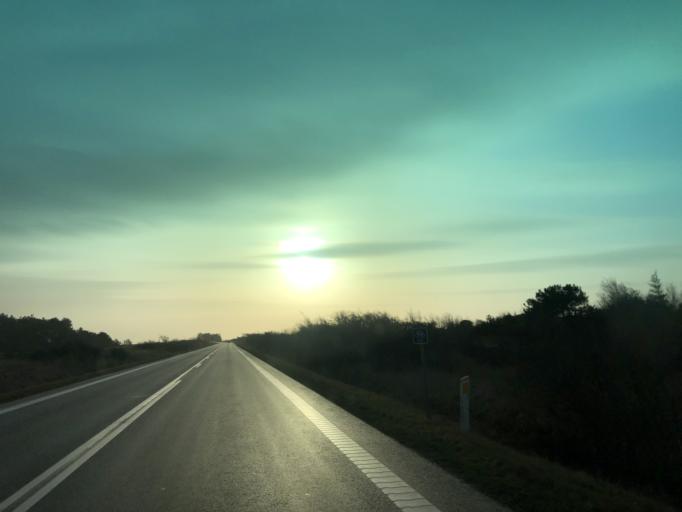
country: DK
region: North Denmark
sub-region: Thisted Kommune
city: Hurup
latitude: 56.6757
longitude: 8.3993
